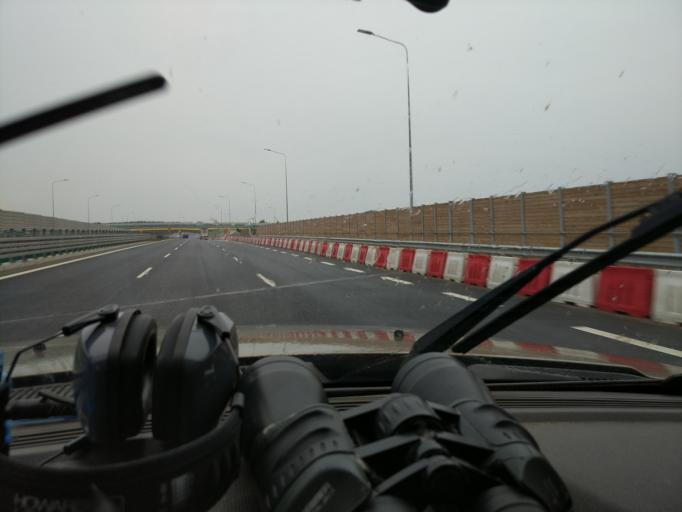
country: PL
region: Masovian Voivodeship
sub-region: Powiat wolominski
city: Kobylka
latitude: 52.3686
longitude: 21.1891
